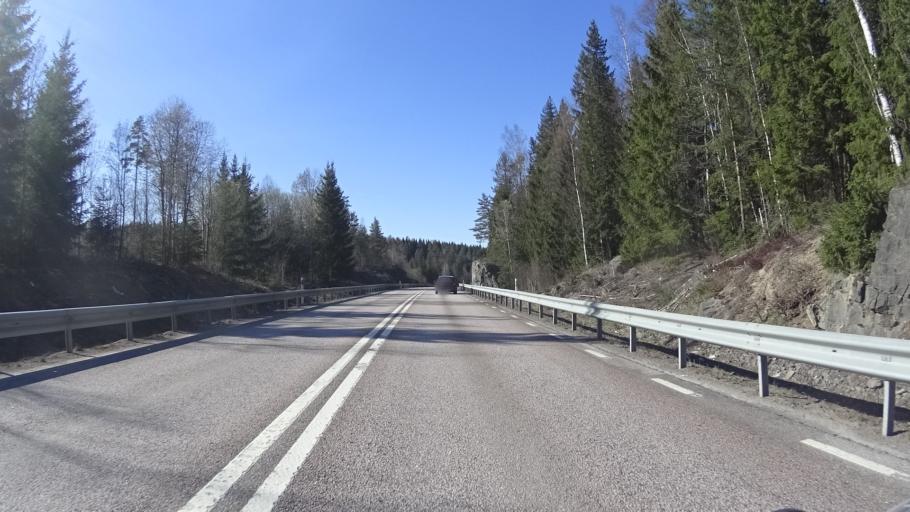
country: SE
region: Vaermland
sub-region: Karlstads Kommun
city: Edsvalla
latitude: 59.5445
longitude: 13.0710
